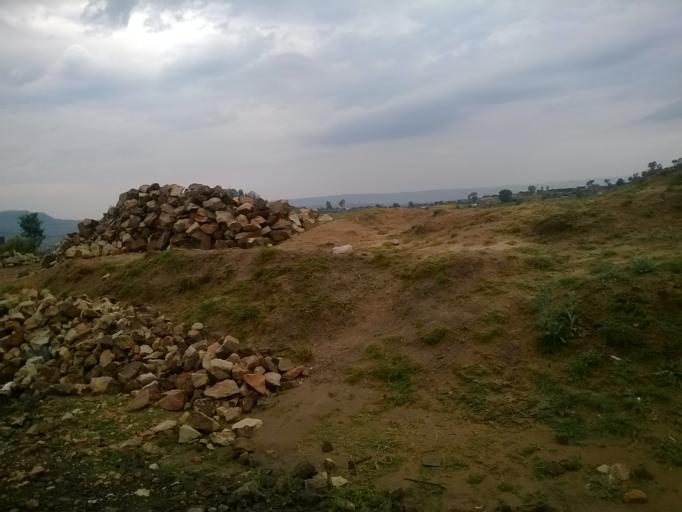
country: LS
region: Berea
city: Teyateyaneng
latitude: -29.1364
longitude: 27.7393
